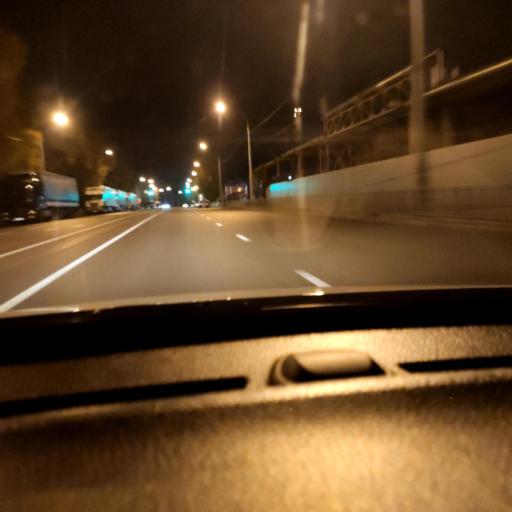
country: RU
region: Voronezj
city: Maslovka
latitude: 51.6024
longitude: 39.2438
